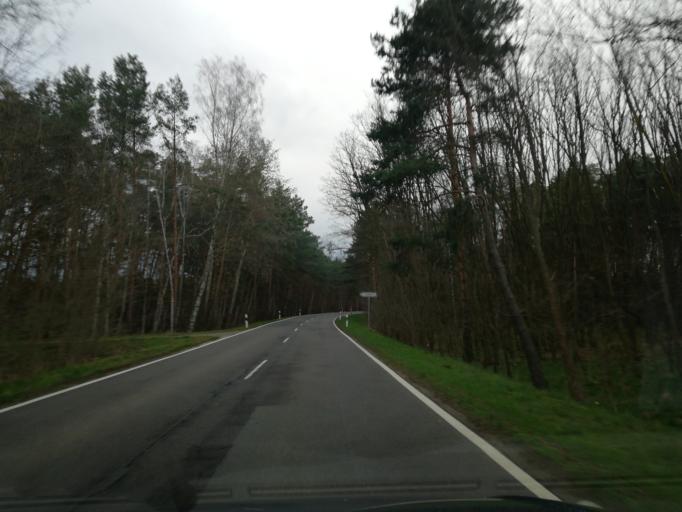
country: DE
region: Brandenburg
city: Vetschau
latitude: 51.7627
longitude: 14.0623
